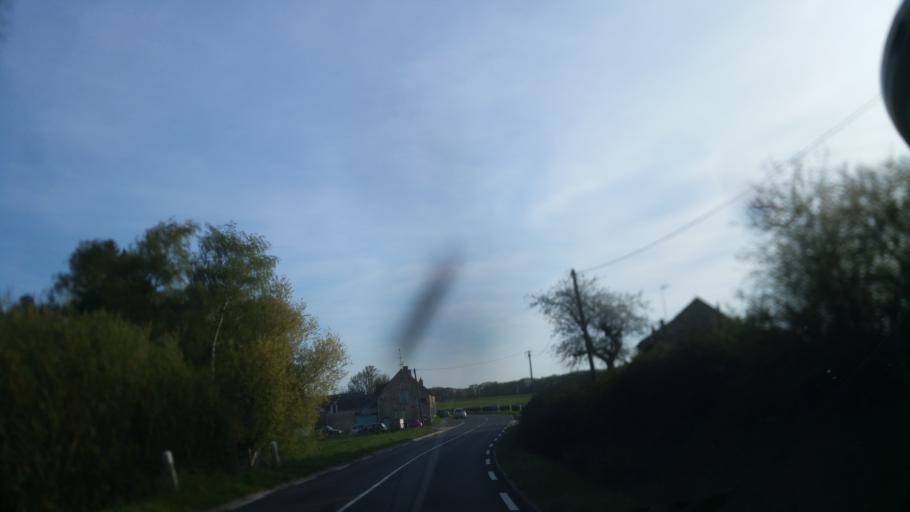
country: FR
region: Ile-de-France
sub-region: Departement de l'Essonne
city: Dourdan
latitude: 48.5455
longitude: 2.0194
